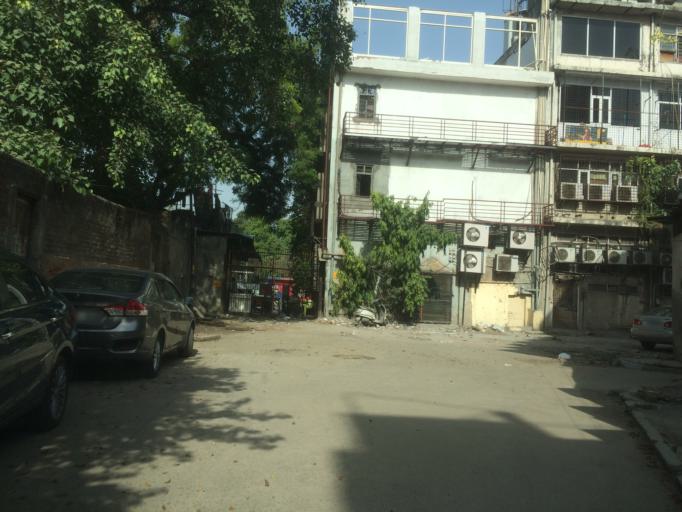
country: IN
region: NCT
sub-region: New Delhi
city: New Delhi
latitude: 28.5660
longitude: 77.2470
